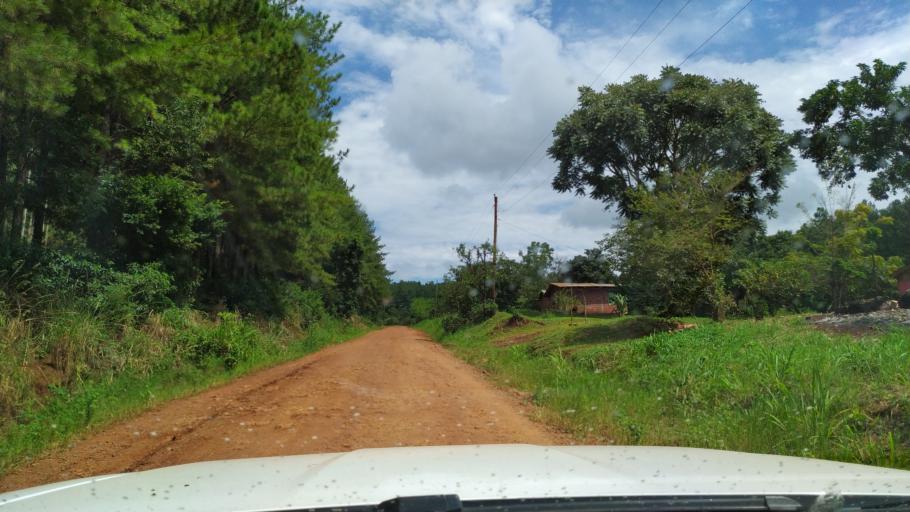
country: AR
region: Misiones
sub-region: Departamento de Eldorado
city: Eldorado
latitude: -26.4982
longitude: -54.5888
